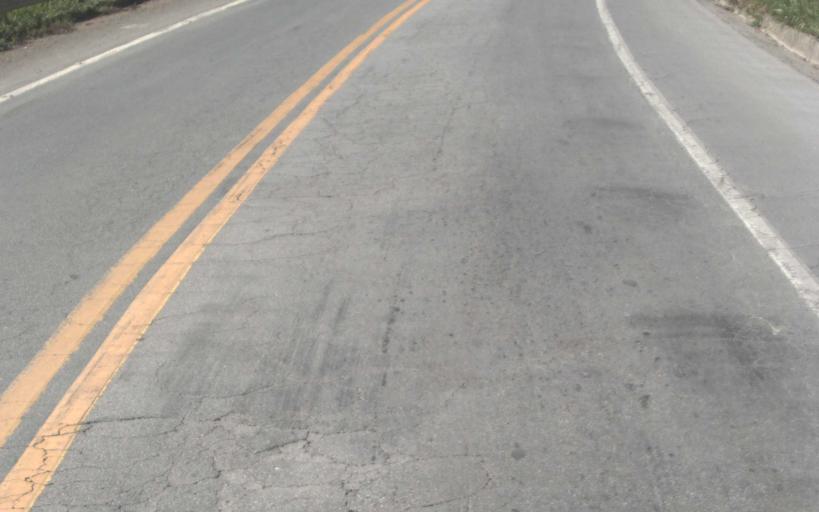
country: BR
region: Minas Gerais
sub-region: Ipaba
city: Ipaba
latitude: -19.3257
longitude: -42.4190
